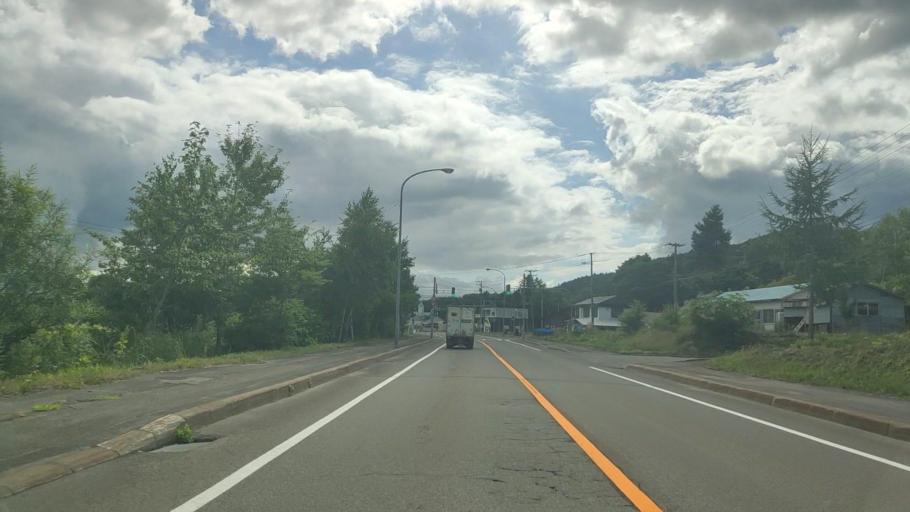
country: JP
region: Hokkaido
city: Shiraoi
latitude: 42.6744
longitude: 141.0841
